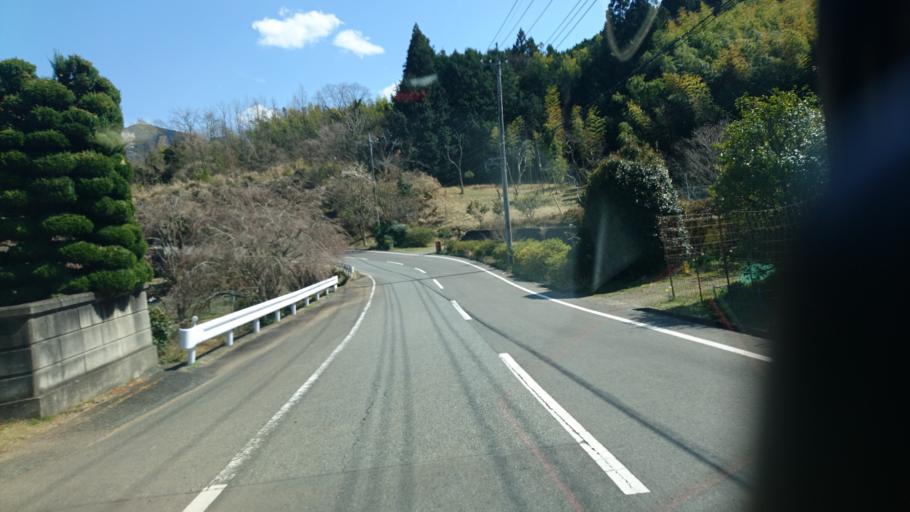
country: JP
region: Shizuoka
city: Fujinomiya
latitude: 35.3414
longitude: 138.4409
